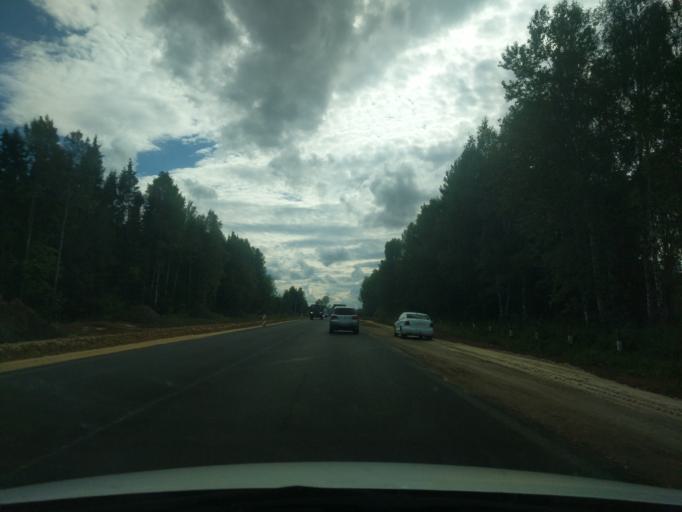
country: RU
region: Jaroslavl
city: Levashevo
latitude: 57.6622
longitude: 40.5701
